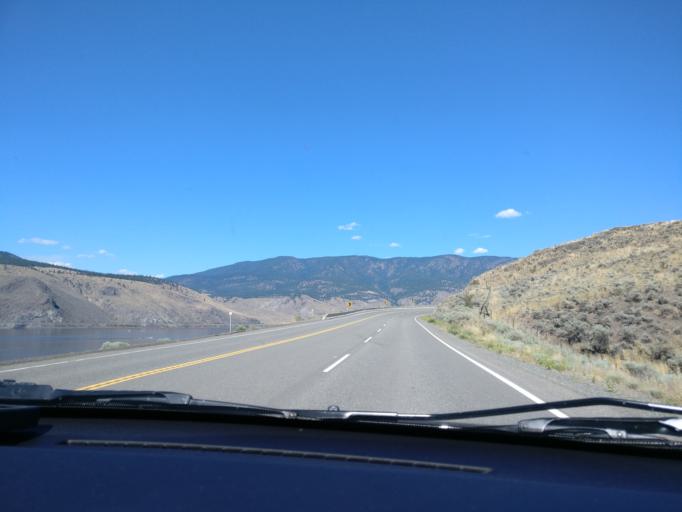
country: CA
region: British Columbia
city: Logan Lake
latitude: 50.7630
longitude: -120.7924
